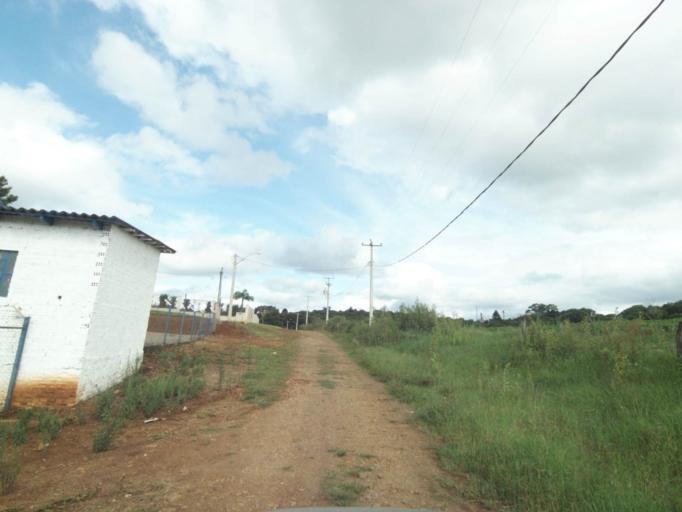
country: BR
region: Rio Grande do Sul
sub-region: Lagoa Vermelha
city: Lagoa Vermelha
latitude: -28.2048
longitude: -51.5428
